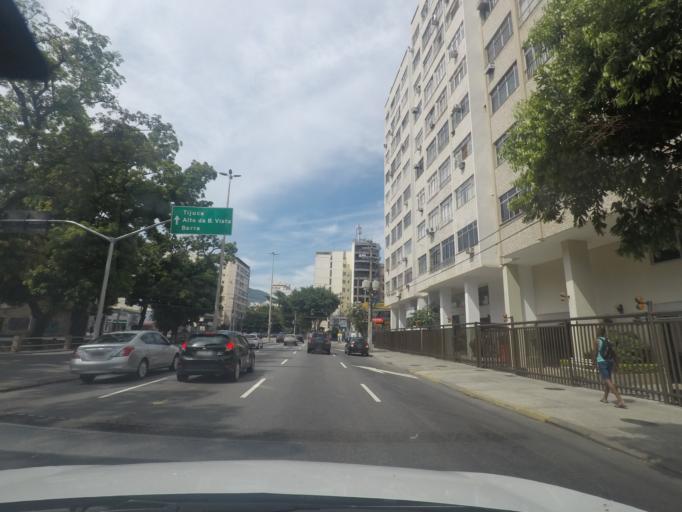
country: BR
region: Rio de Janeiro
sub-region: Rio De Janeiro
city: Rio de Janeiro
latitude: -22.9156
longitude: -43.2293
